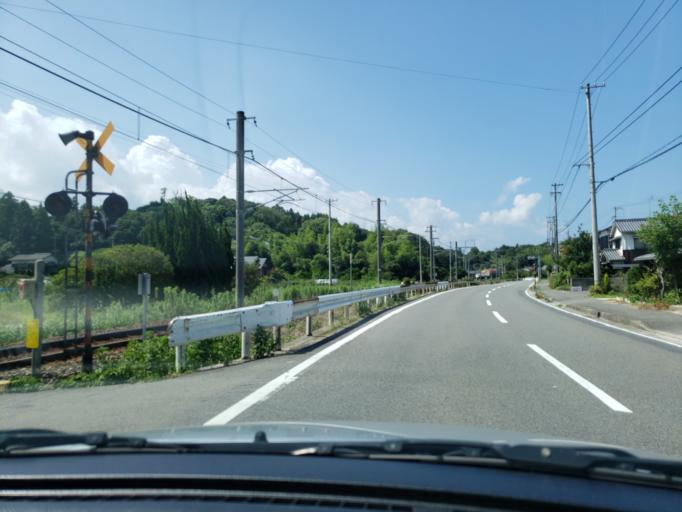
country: JP
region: Ehime
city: Hojo
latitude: 34.0884
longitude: 132.9315
